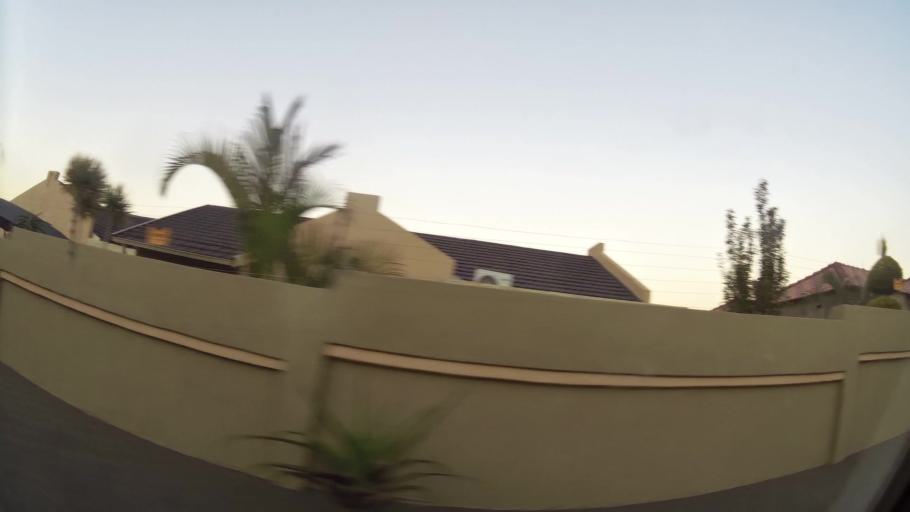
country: ZA
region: North-West
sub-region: Bojanala Platinum District Municipality
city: Rustenburg
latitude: -25.6548
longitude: 27.2064
